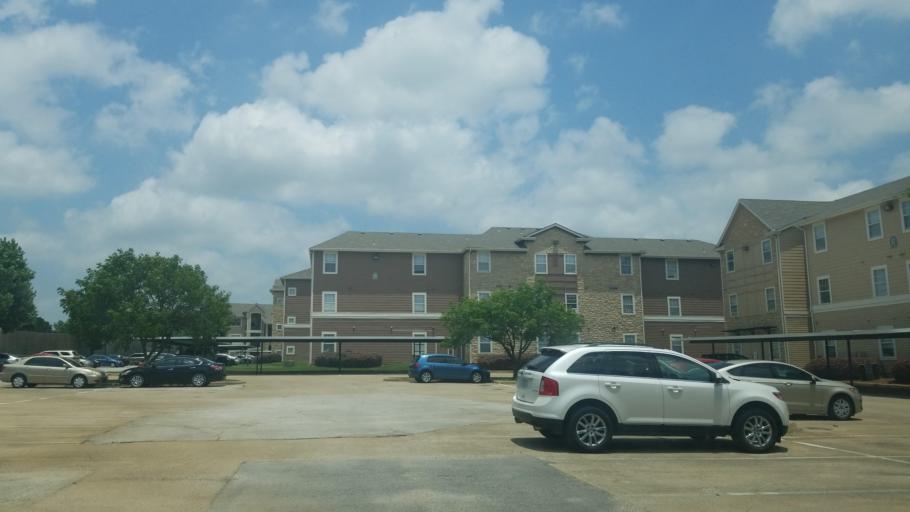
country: US
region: Texas
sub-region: Denton County
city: Denton
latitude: 33.1854
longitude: -97.1024
